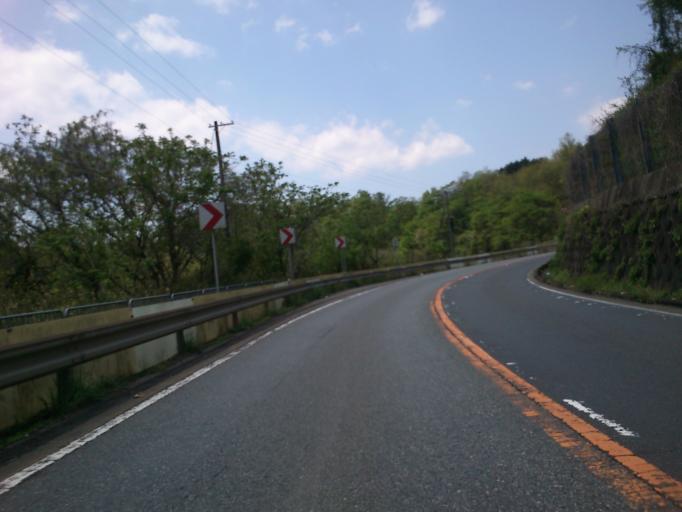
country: JP
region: Kyoto
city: Fukuchiyama
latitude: 35.3293
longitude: 134.9420
